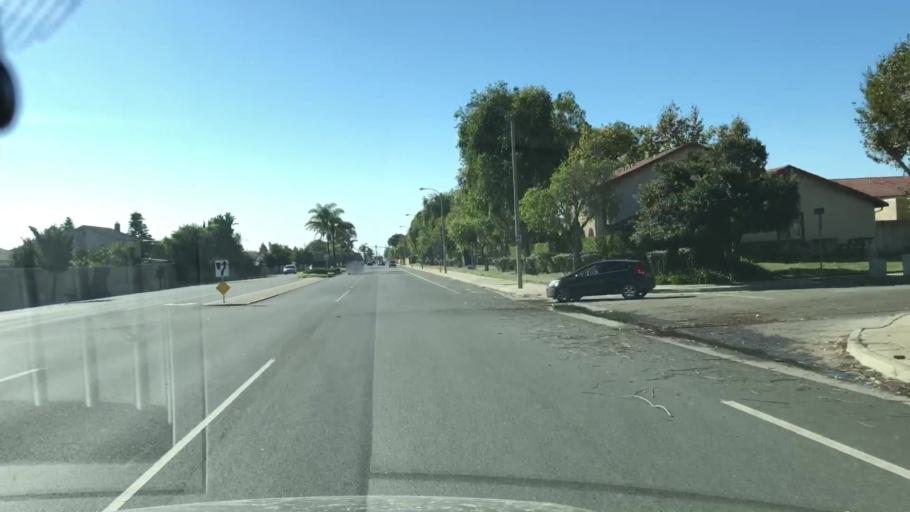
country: US
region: California
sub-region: Ventura County
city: Oxnard Shores
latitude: 34.1904
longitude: -119.2111
